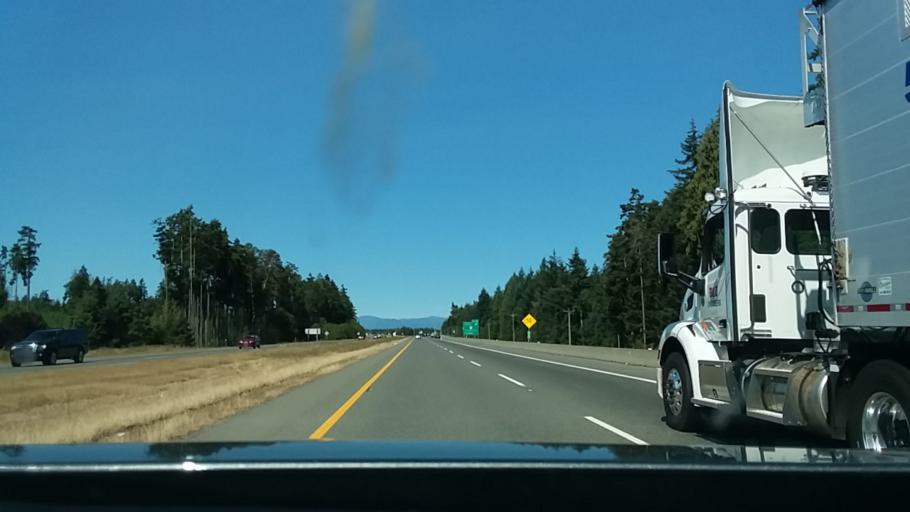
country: CA
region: British Columbia
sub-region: Regional District of Nanaimo
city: Parksville
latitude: 49.3036
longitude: -124.3106
